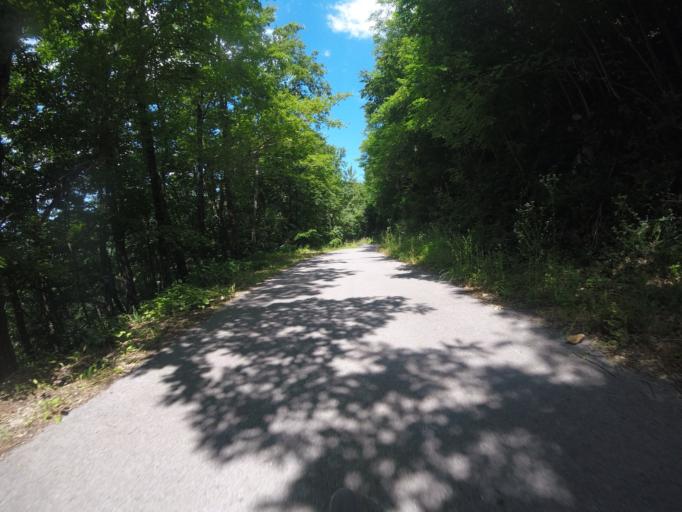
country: SI
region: Kostanjevica na Krki
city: Kostanjevica na Krki
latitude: 45.7642
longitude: 15.4204
